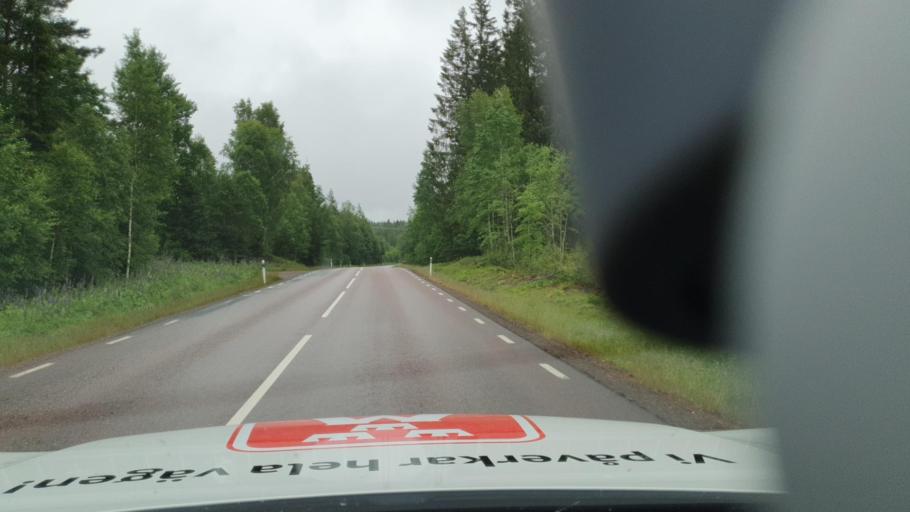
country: SE
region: Vaermland
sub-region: Kristinehamns Kommun
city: Bjorneborg
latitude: 59.2361
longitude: 14.2865
